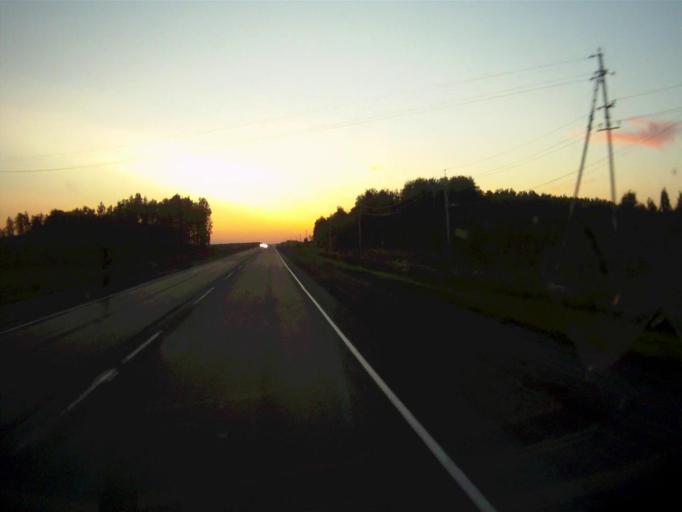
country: RU
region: Chelyabinsk
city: Poletayevo
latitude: 55.2128
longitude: 61.0687
